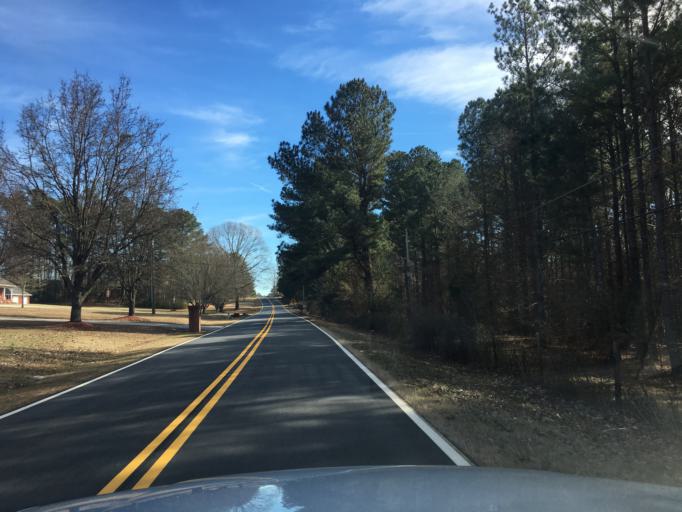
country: US
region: Georgia
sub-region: Rockdale County
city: Lakeview Estates
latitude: 33.7353
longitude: -84.0315
